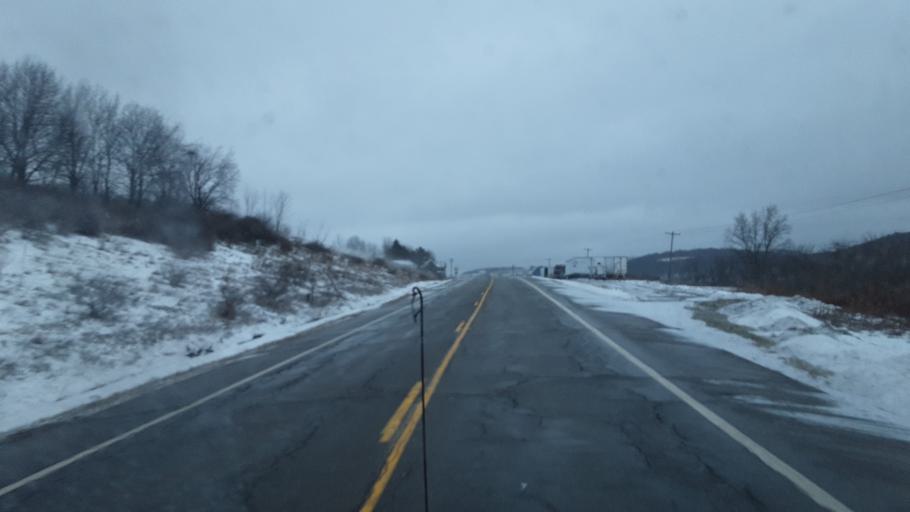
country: US
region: New York
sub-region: Steuben County
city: Canisteo
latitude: 42.1365
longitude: -77.5166
